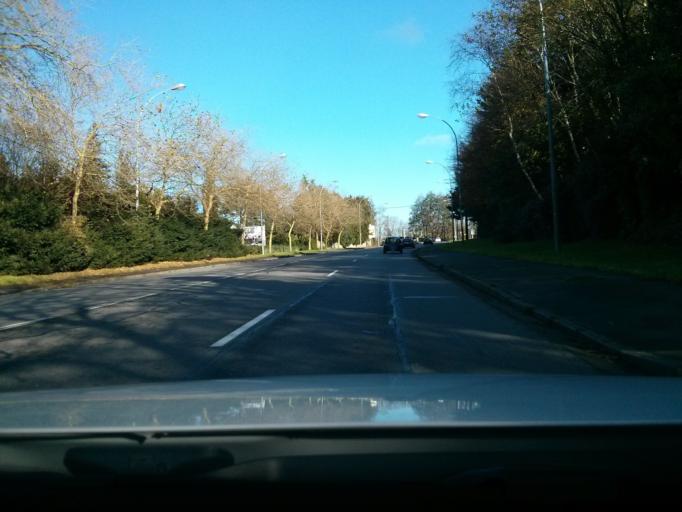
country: FR
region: Brittany
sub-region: Departement du Finistere
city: Bohars
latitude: 48.4117
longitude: -4.5109
